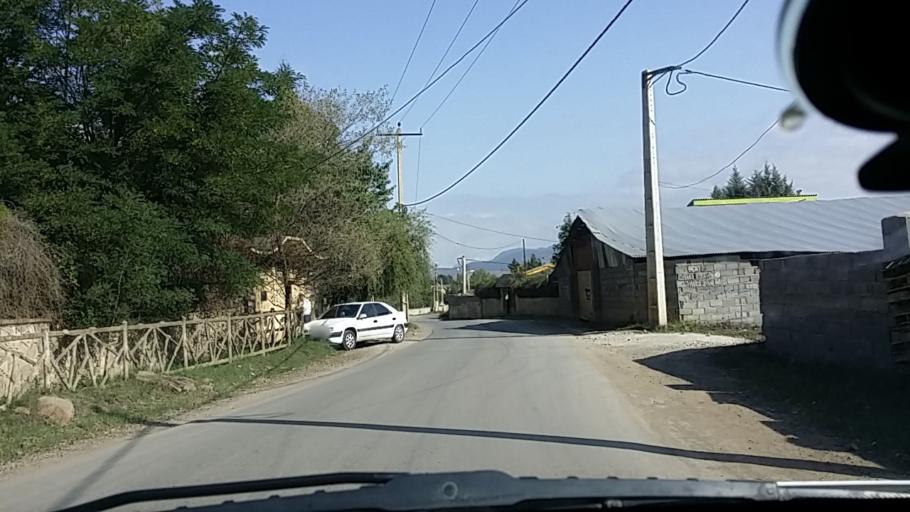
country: IR
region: Mazandaran
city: `Abbasabad
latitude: 36.5036
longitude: 51.1725
